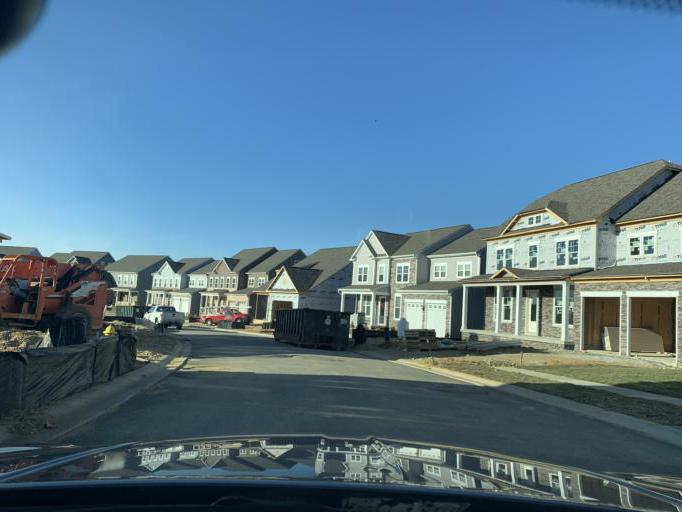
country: US
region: Maryland
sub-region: Anne Arundel County
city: Crofton
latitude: 39.0232
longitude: -76.7189
